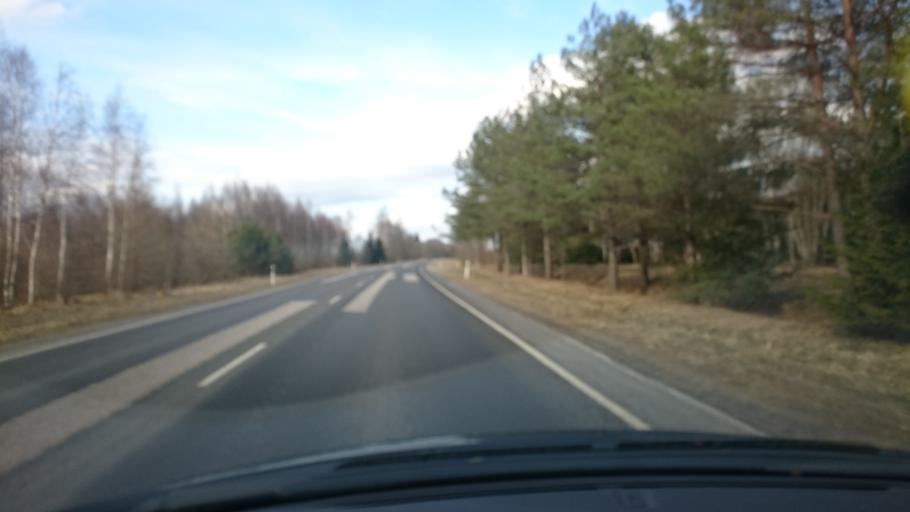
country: EE
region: Harju
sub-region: Nissi vald
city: Turba
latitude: 58.8889
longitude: 24.0927
